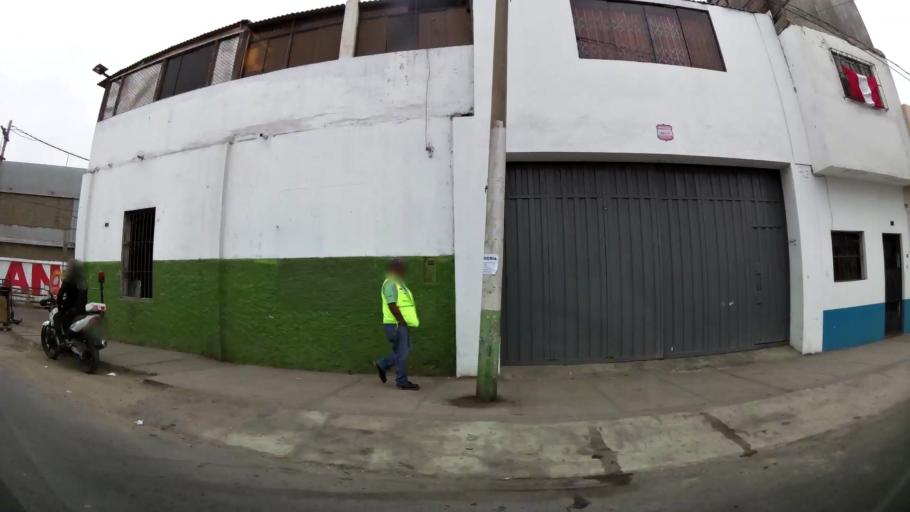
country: PE
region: Callao
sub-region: Callao
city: Callao
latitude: -12.0520
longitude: -77.1364
